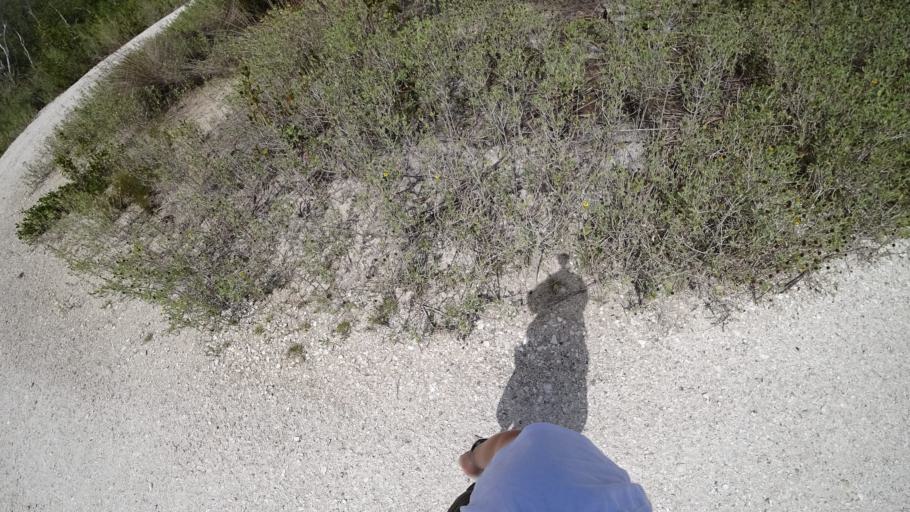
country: US
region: Florida
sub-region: Manatee County
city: Cortez
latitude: 27.4948
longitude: -82.6850
